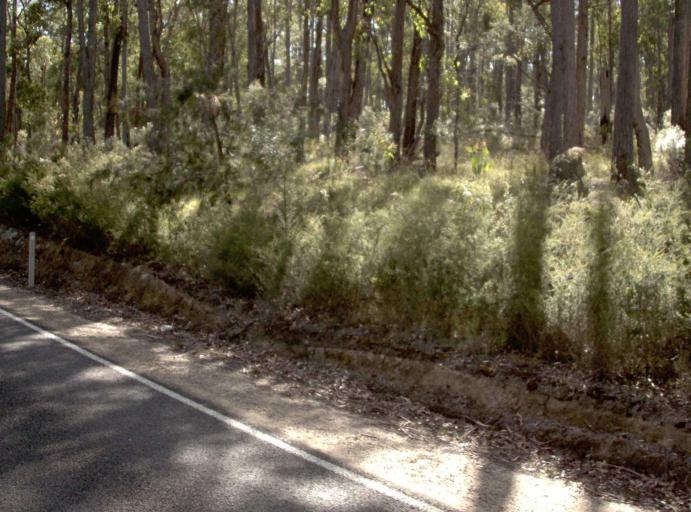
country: AU
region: Victoria
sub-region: East Gippsland
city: Lakes Entrance
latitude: -37.5514
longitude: 148.1467
